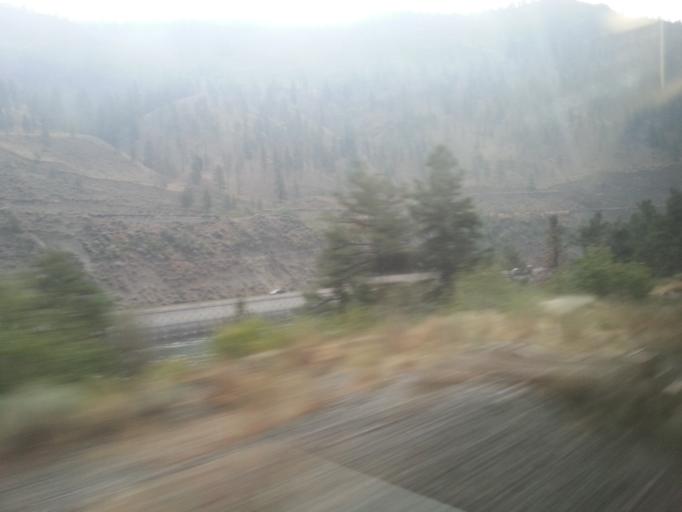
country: CA
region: British Columbia
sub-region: Thompson-Nicola Regional District
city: Ashcroft
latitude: 50.3228
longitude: -121.3943
